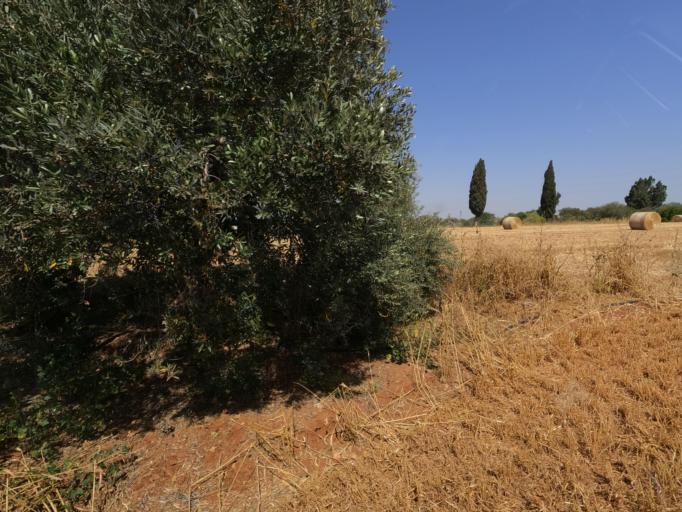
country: CY
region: Ammochostos
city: Frenaros
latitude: 35.0010
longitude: 33.9440
